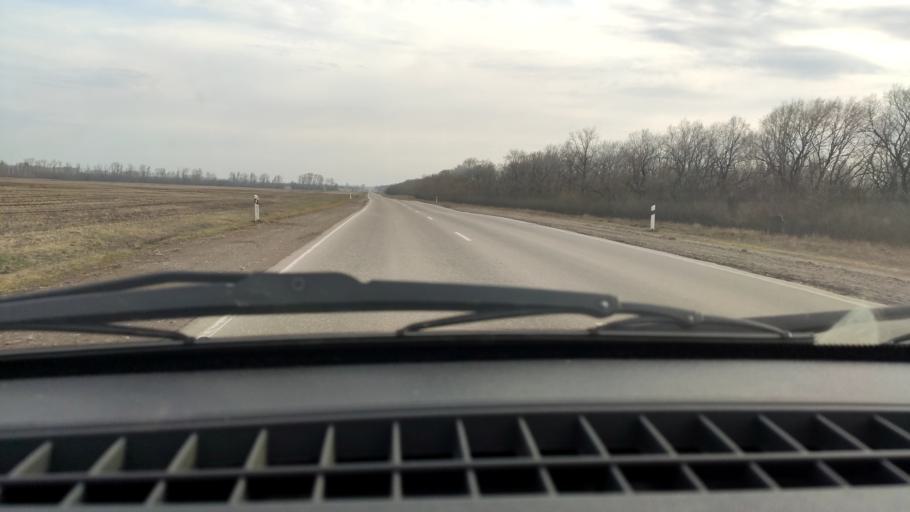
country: RU
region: Bashkortostan
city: Davlekanovo
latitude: 54.2483
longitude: 55.0785
